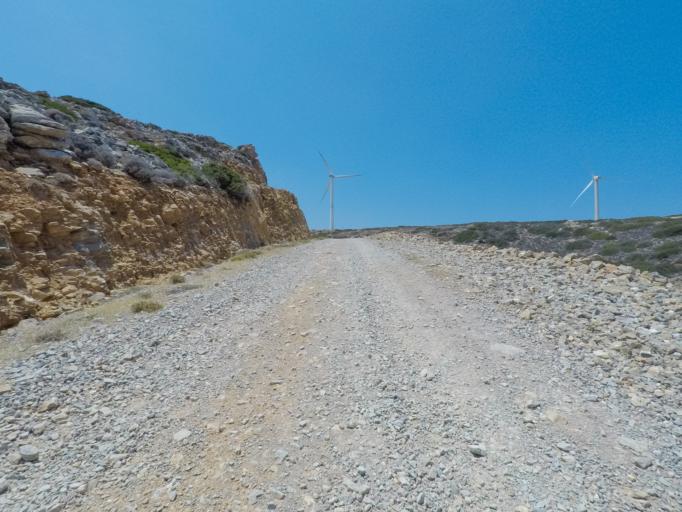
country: GR
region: Crete
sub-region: Nomos Lasithiou
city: Elounda
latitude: 35.3281
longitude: 25.7605
